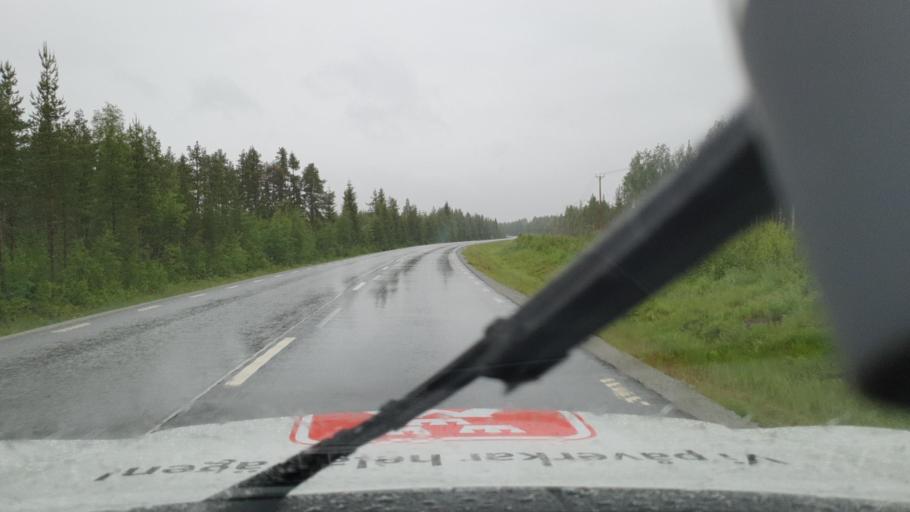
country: SE
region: Vaesterbotten
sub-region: Asele Kommun
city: Insjon
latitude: 64.1334
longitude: 18.0512
